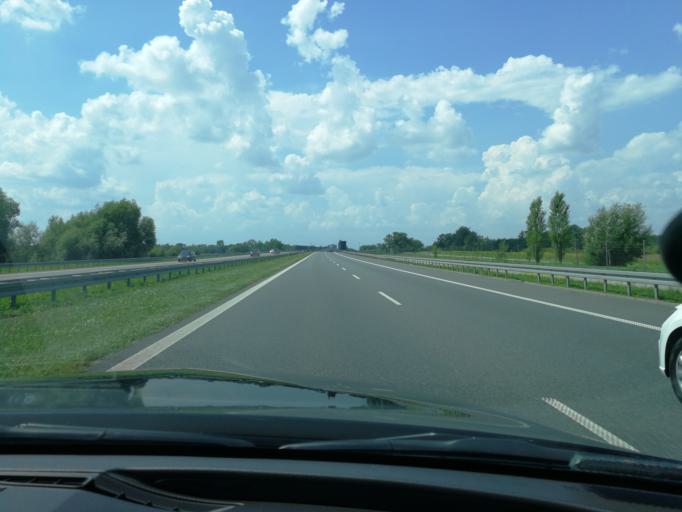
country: PL
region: Masovian Voivodeship
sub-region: Powiat warszawski zachodni
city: Bieniewice
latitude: 52.1213
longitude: 20.5166
